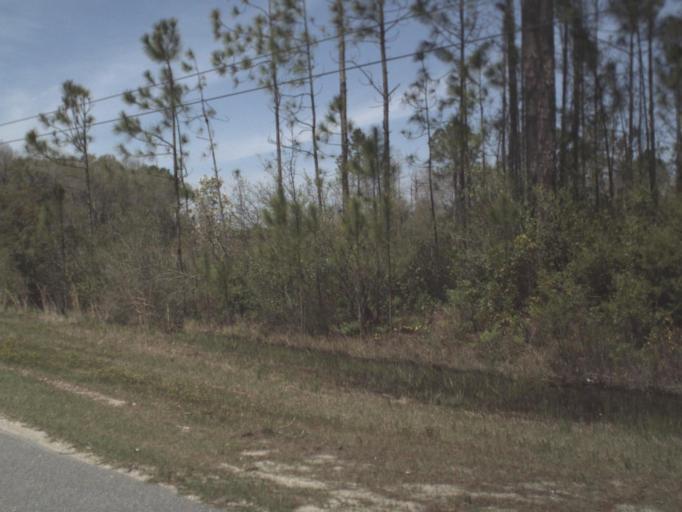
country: US
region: Florida
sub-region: Bay County
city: Lynn Haven
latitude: 30.3288
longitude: -85.7295
